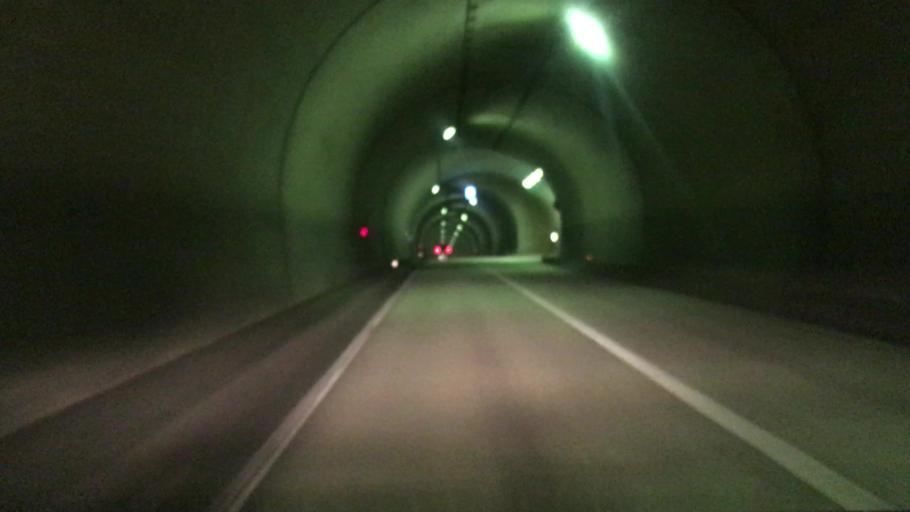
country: JP
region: Hyogo
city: Toyooka
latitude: 35.4182
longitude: 134.7403
